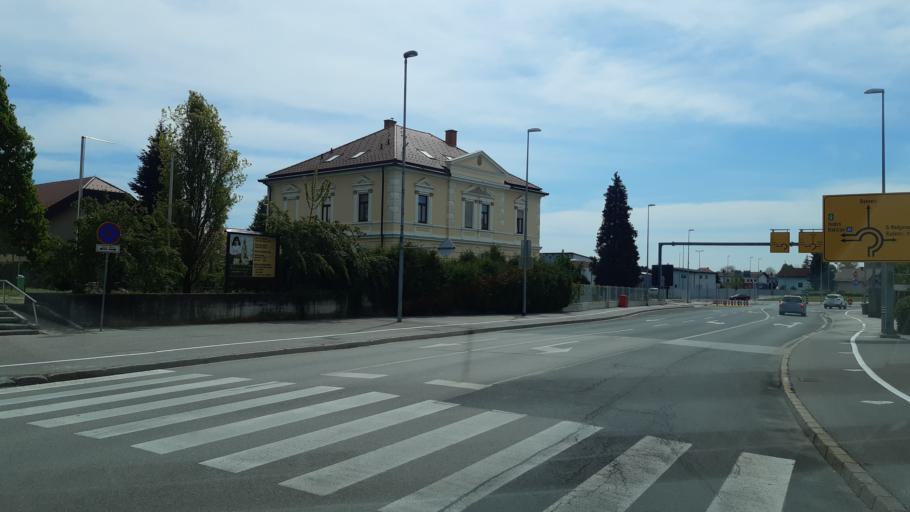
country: SI
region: Murska Sobota
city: Murska Sobota
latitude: 46.6579
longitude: 16.1691
